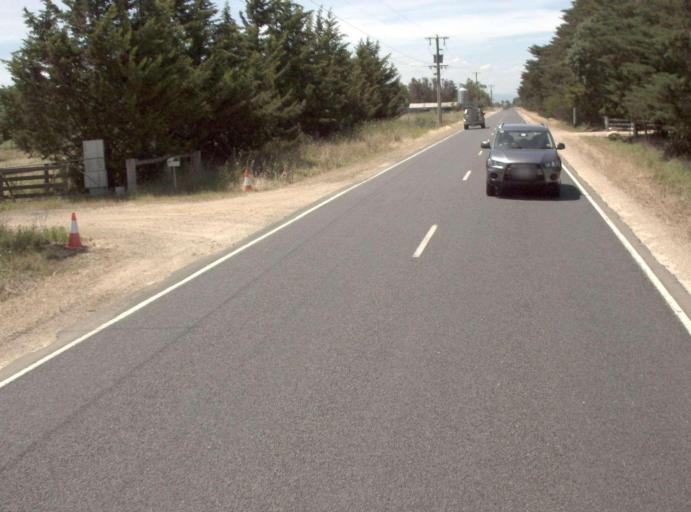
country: AU
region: Victoria
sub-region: Wellington
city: Heyfield
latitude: -38.0313
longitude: 146.8791
